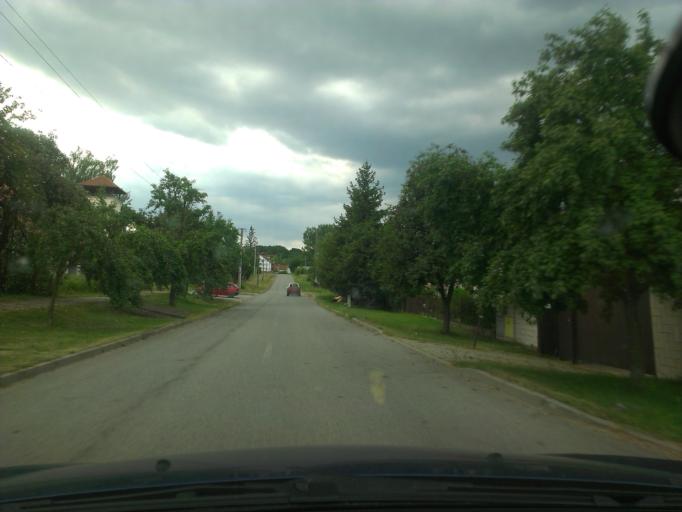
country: CZ
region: South Moravian
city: Velka nad Velickou
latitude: 48.8639
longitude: 17.5263
